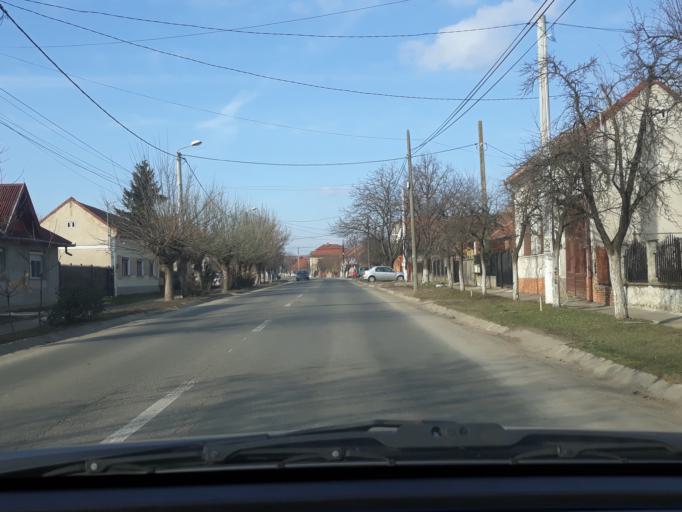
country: RO
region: Bihor
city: Margita
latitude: 47.3529
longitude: 22.3389
